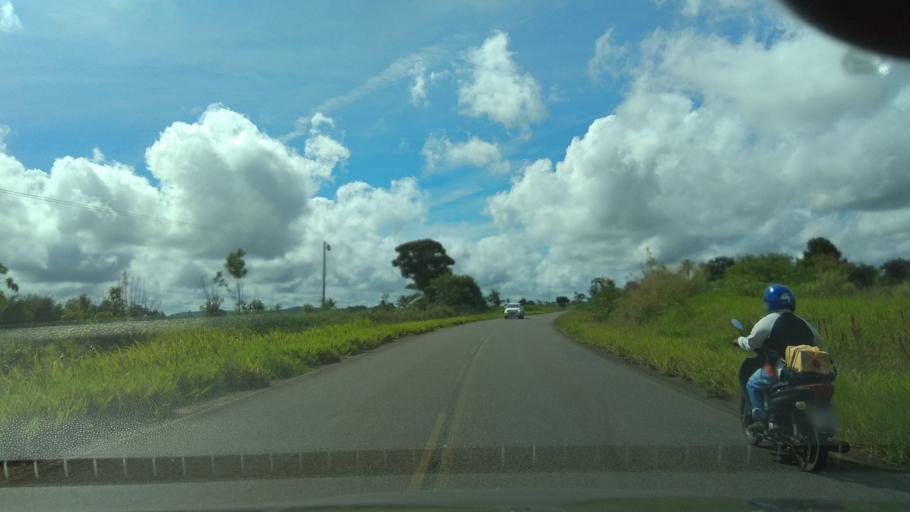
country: BR
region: Bahia
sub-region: Mutuipe
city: Mutuipe
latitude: -13.1673
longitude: -39.3408
